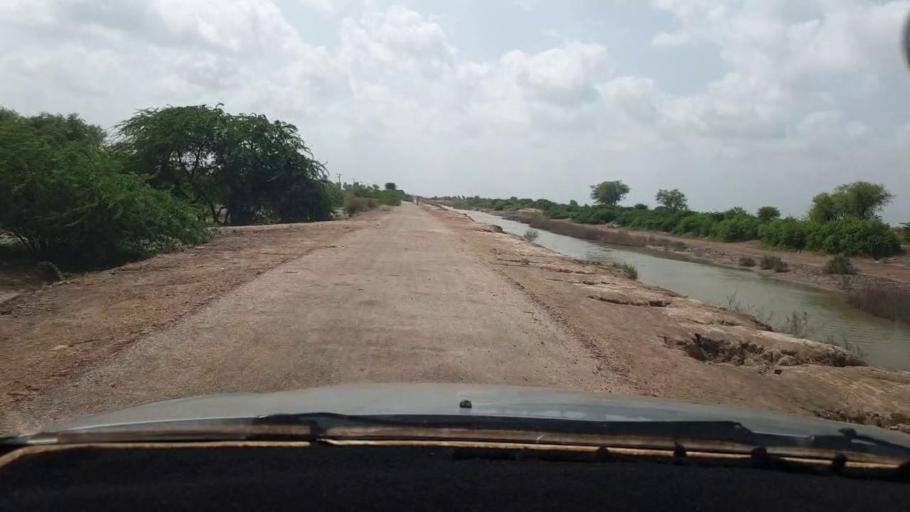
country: PK
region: Sindh
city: Tando Bago
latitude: 24.7228
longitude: 69.1356
